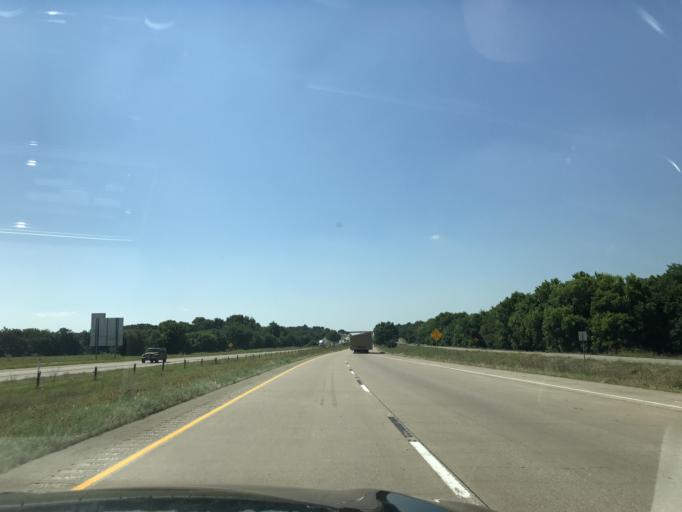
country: US
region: Texas
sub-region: Johnson County
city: Alvarado
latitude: 32.3890
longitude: -97.2088
